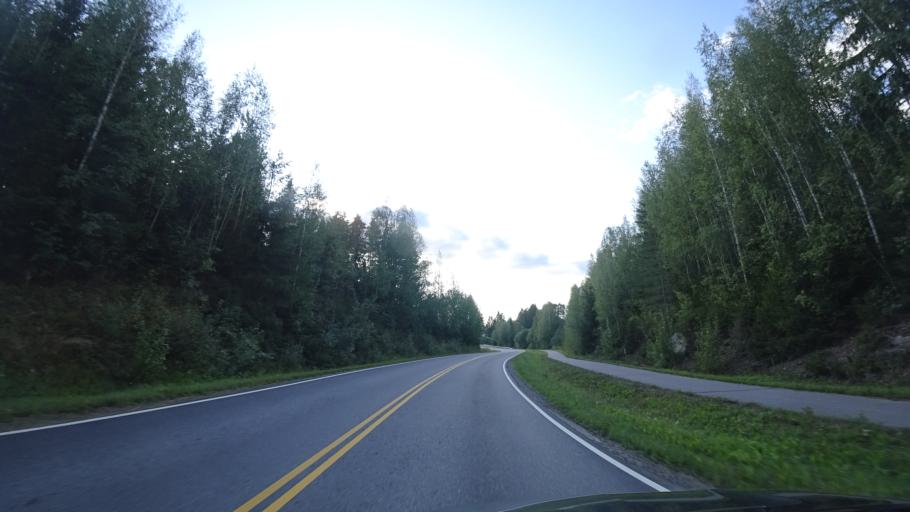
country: FI
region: Haeme
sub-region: Haemeenlinna
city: Lammi
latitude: 61.0806
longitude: 25.0642
